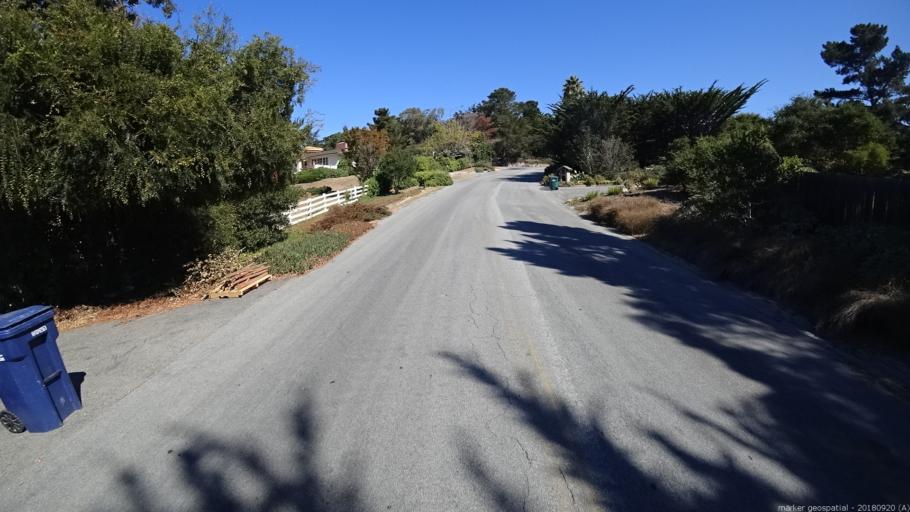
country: US
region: California
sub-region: Monterey County
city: Carmel-by-the-Sea
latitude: 36.5462
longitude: -121.9023
